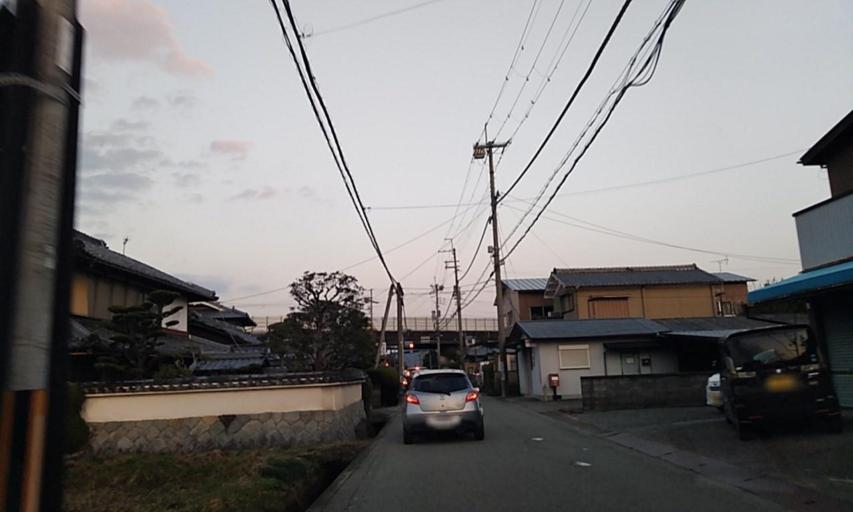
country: JP
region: Kyoto
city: Kameoka
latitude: 35.0181
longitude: 135.5525
